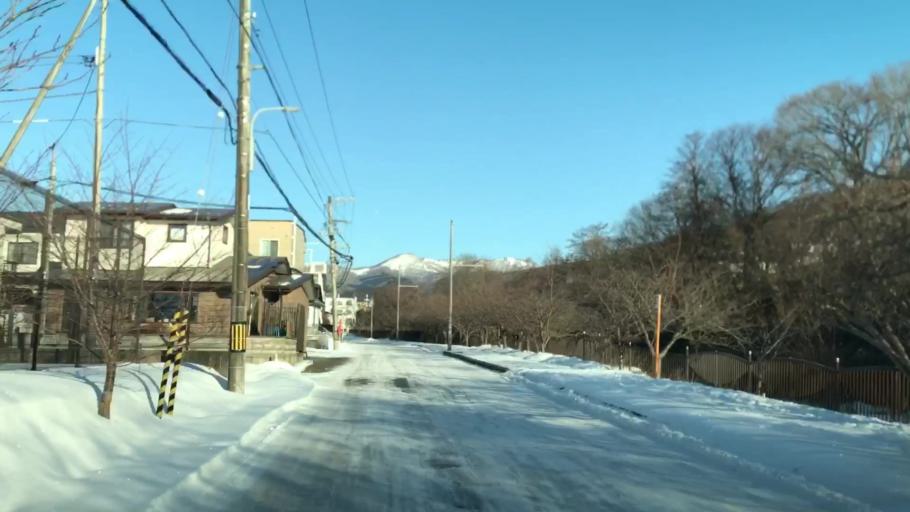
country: JP
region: Hokkaido
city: Muroran
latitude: 42.3729
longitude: 141.0380
